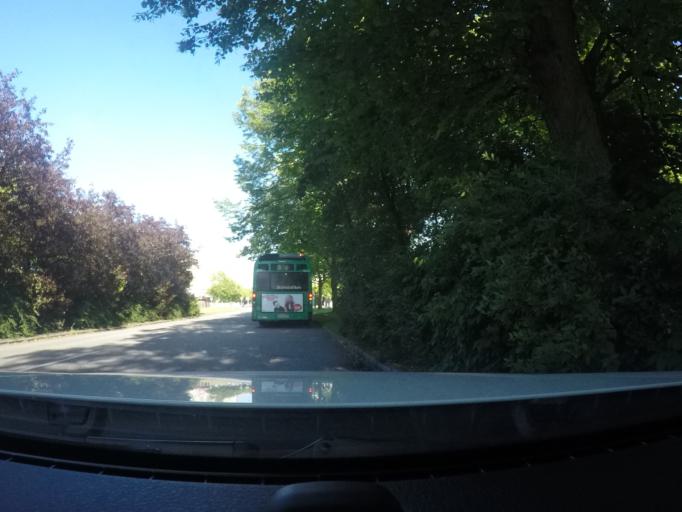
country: SE
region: Skane
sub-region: Malmo
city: Tygelsjo
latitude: 55.5587
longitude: 13.0117
